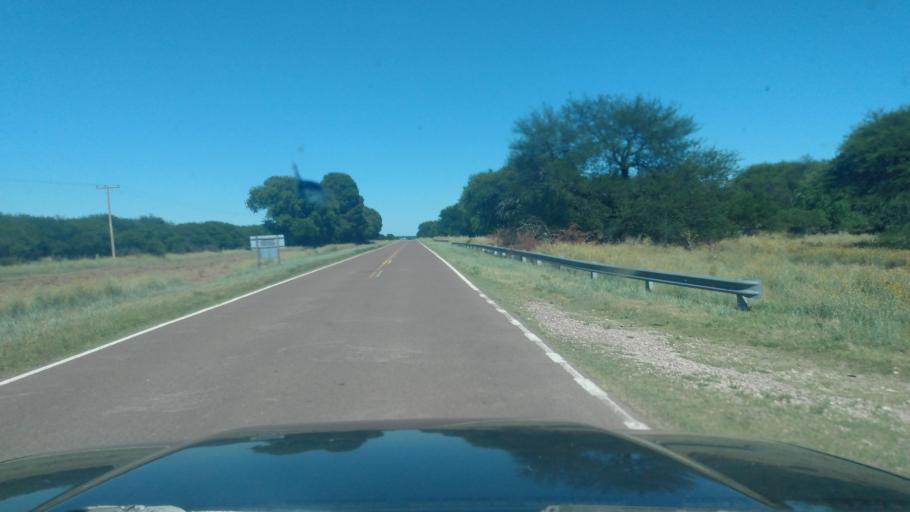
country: AR
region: La Pampa
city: General Acha
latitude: -37.4177
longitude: -64.8555
